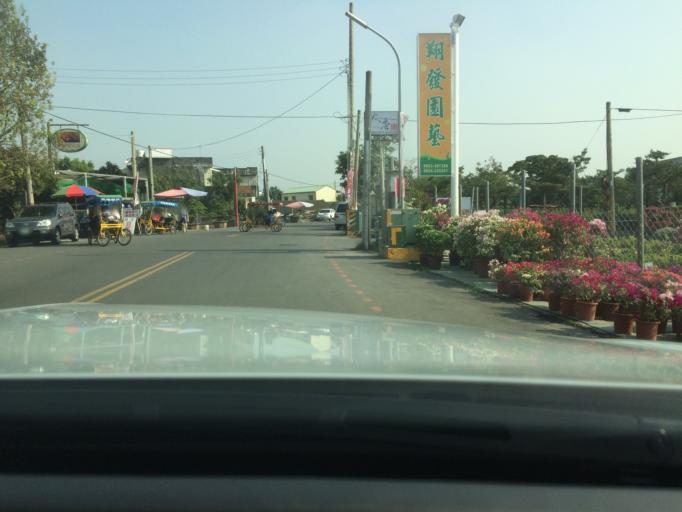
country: TW
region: Taiwan
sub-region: Nantou
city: Nantou
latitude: 23.9012
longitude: 120.5270
